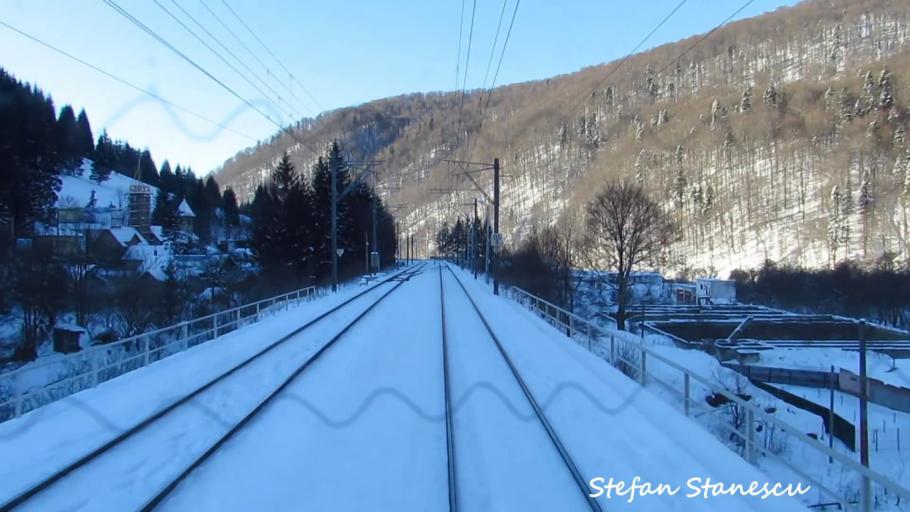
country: RO
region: Prahova
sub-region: Oras Azuga
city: Azuga
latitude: 45.4334
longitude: 25.5520
